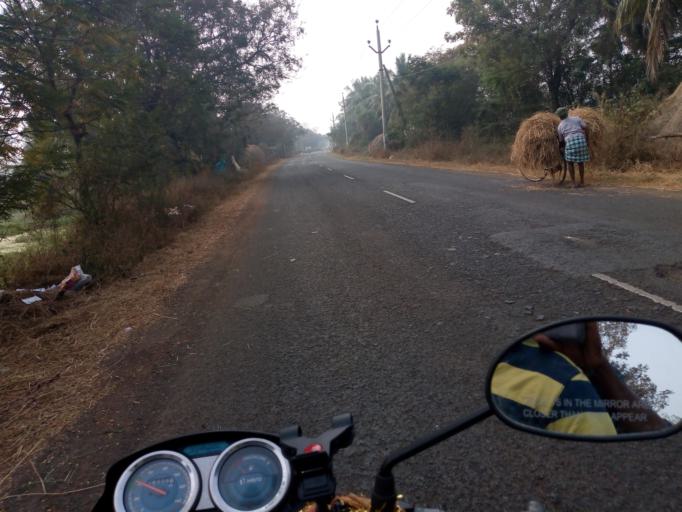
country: IN
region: Andhra Pradesh
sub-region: West Godavari
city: Tadepallegudem
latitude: 16.7558
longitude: 81.4235
